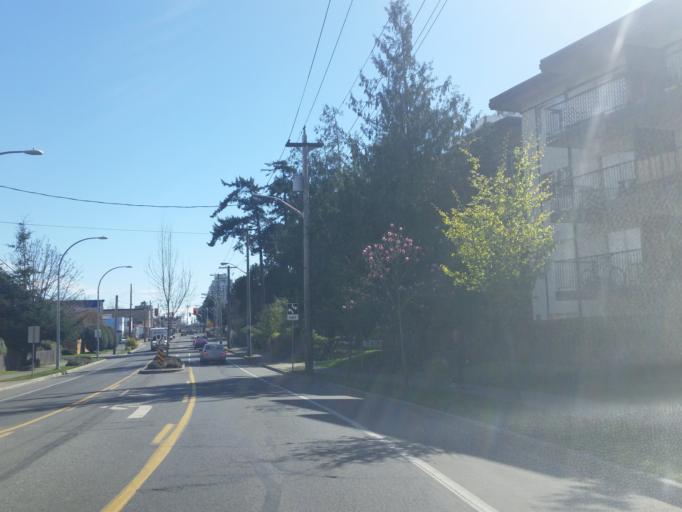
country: CA
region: British Columbia
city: Victoria
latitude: 48.4310
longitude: -123.3922
